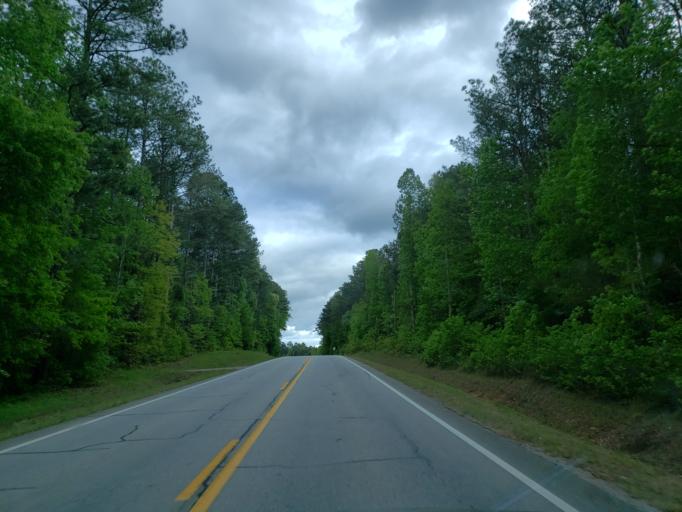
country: US
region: Georgia
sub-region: Haralson County
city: Buchanan
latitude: 33.8162
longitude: -85.1073
